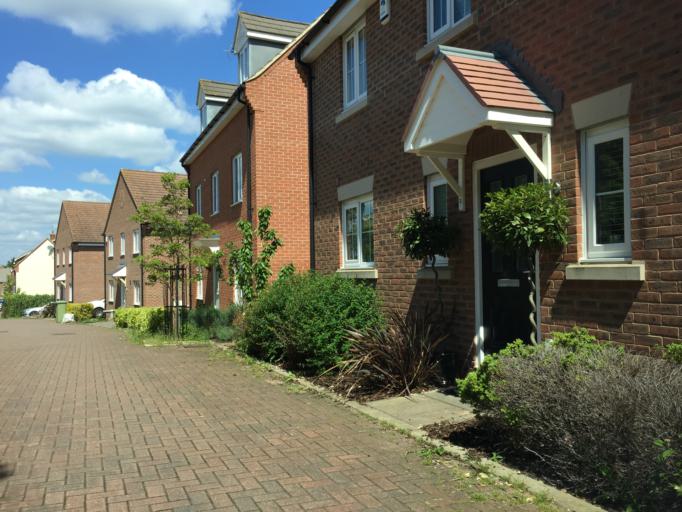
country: GB
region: England
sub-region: Milton Keynes
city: Woburn Sands
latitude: 52.0145
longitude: -0.6563
